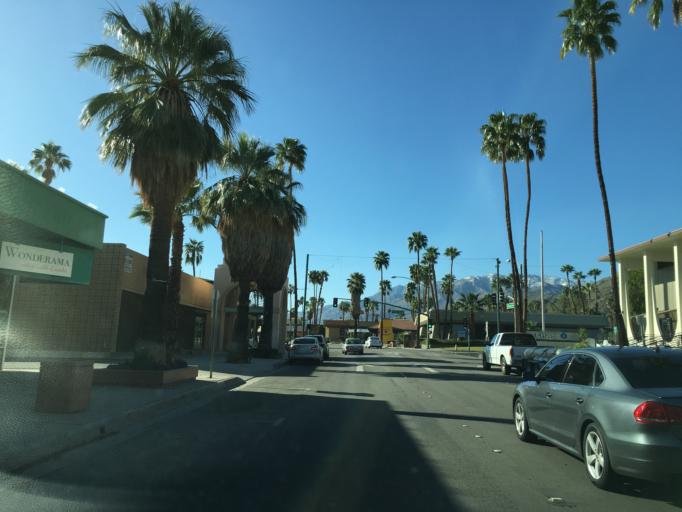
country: US
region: California
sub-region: Riverside County
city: Palm Springs
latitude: 33.8165
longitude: -116.5468
